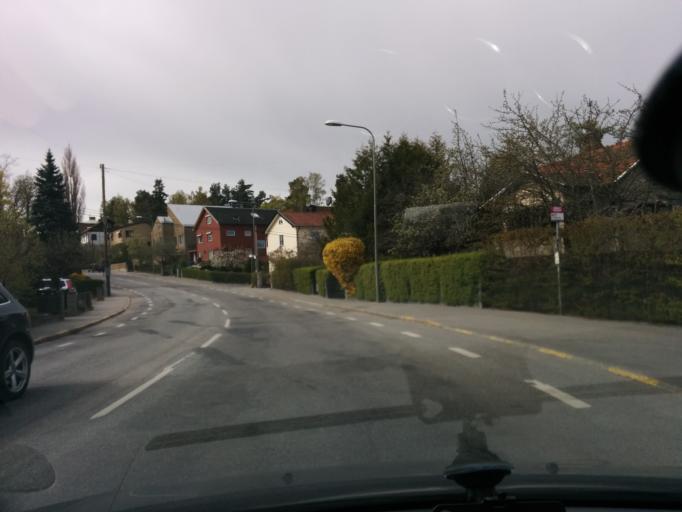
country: SE
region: Stockholm
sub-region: Stockholms Kommun
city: Bromma
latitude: 59.3023
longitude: 17.9802
